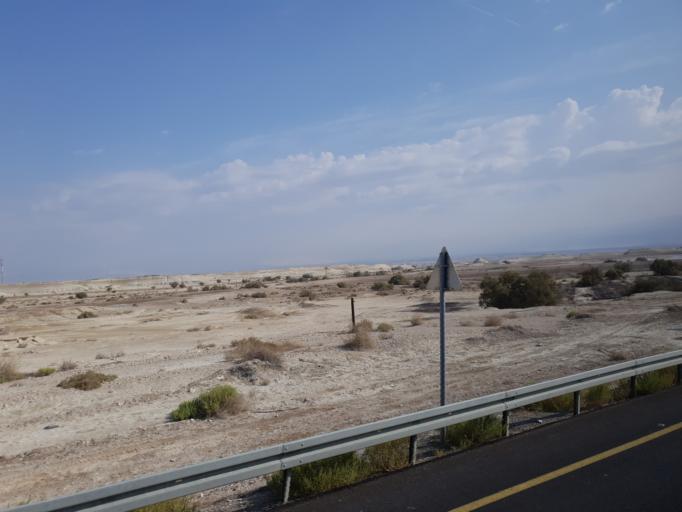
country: PS
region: West Bank
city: Jericho
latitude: 31.7974
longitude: 35.4935
